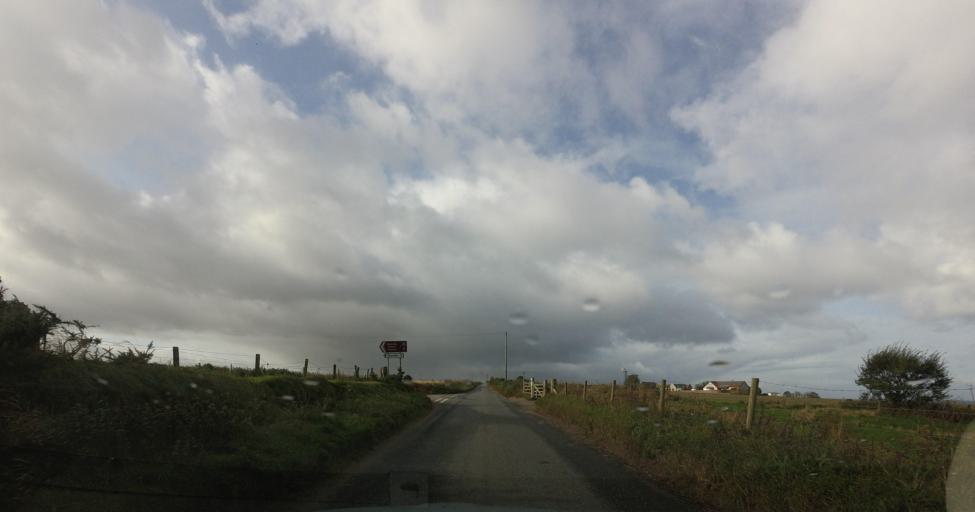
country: GB
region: Scotland
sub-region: Aberdeenshire
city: Whitehills
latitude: 57.6707
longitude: -2.5890
